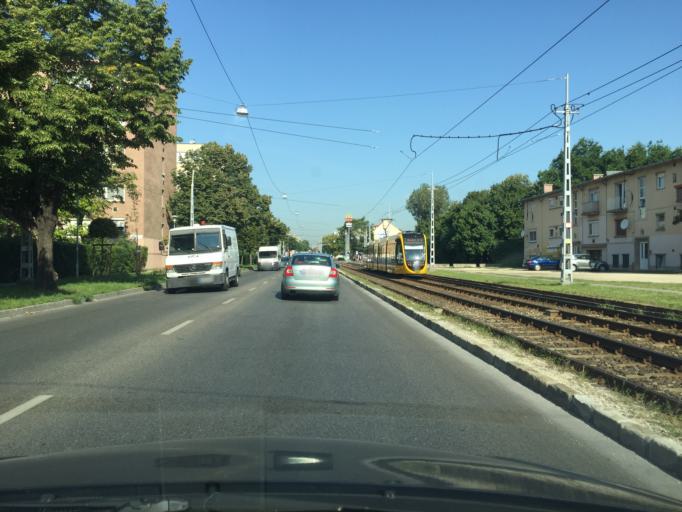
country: HU
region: Budapest
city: Budapest XIV. keruelet
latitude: 47.5135
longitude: 19.1221
